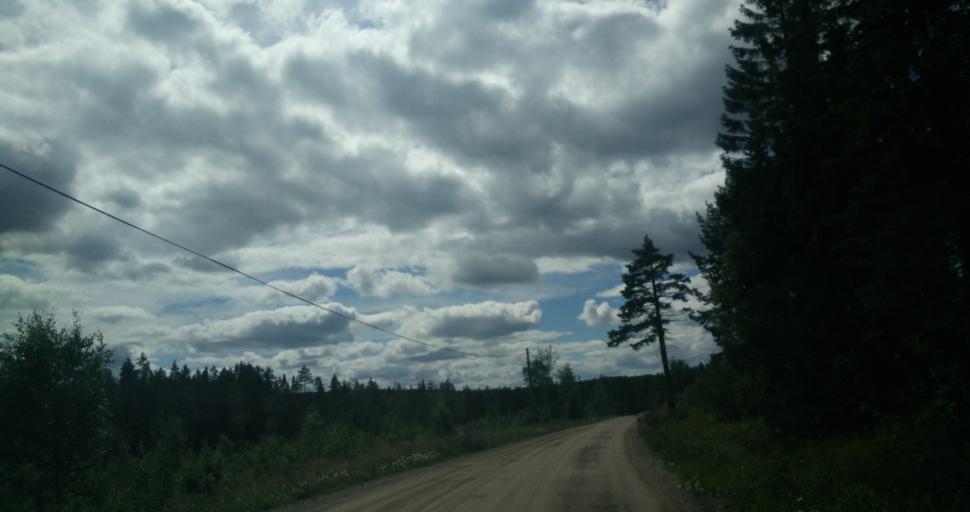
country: SE
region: Gaevleborg
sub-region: Nordanstigs Kommun
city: Bergsjoe
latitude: 62.1331
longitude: 17.1312
